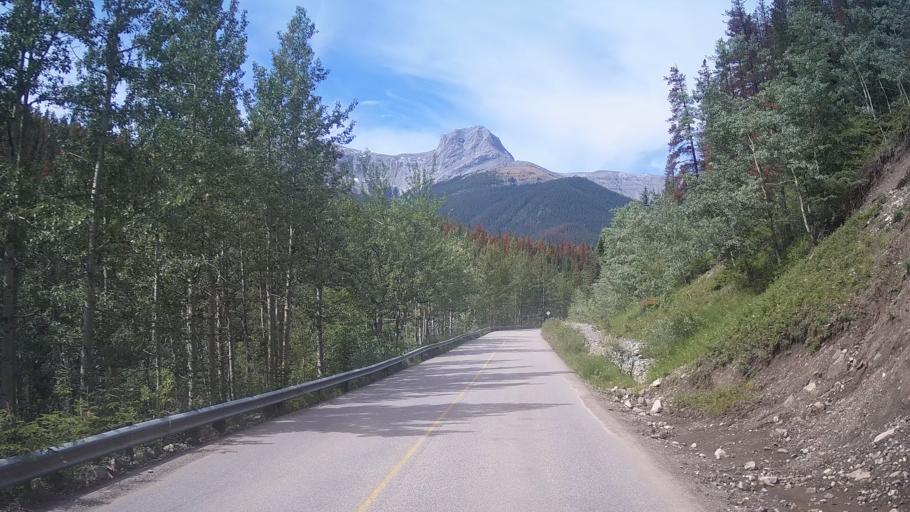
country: CA
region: Alberta
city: Hinton
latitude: 53.1773
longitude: -117.8511
